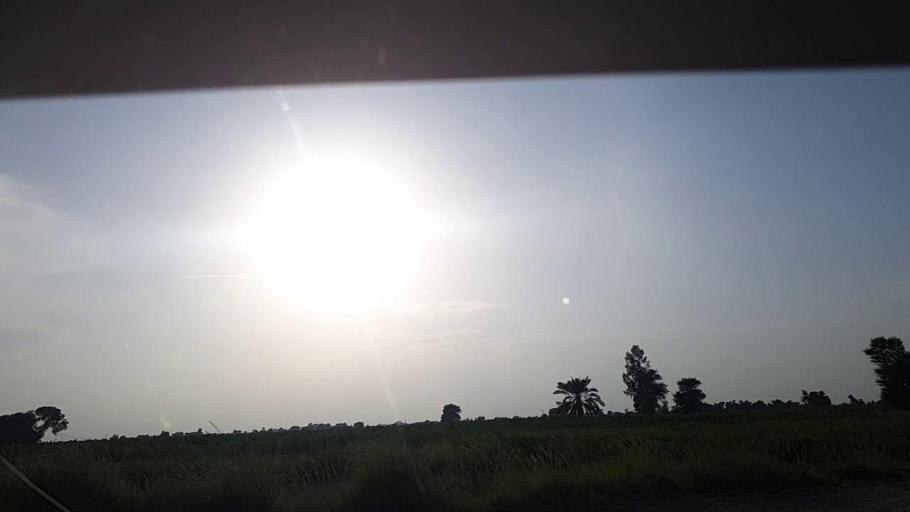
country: PK
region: Sindh
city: Khanpur
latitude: 27.8082
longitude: 69.3248
